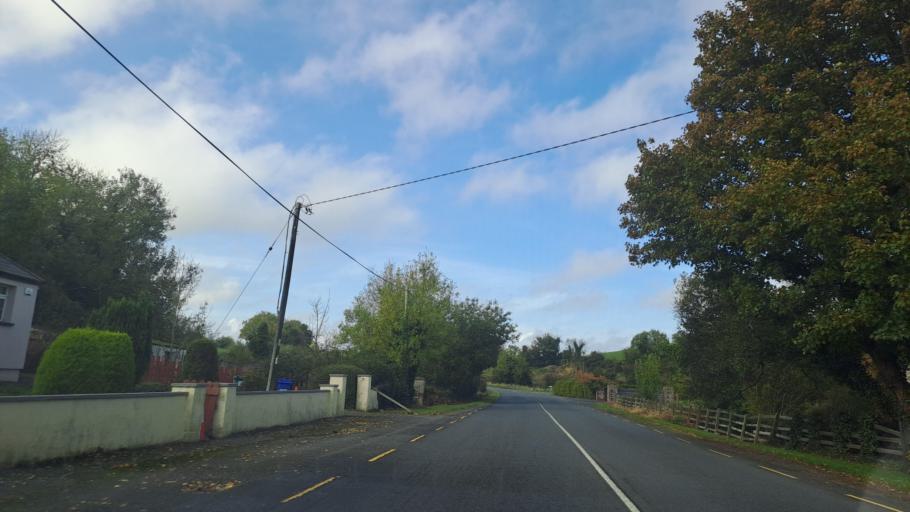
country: IE
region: Ulster
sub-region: An Cabhan
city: Cootehill
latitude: 54.0475
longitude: -7.0045
